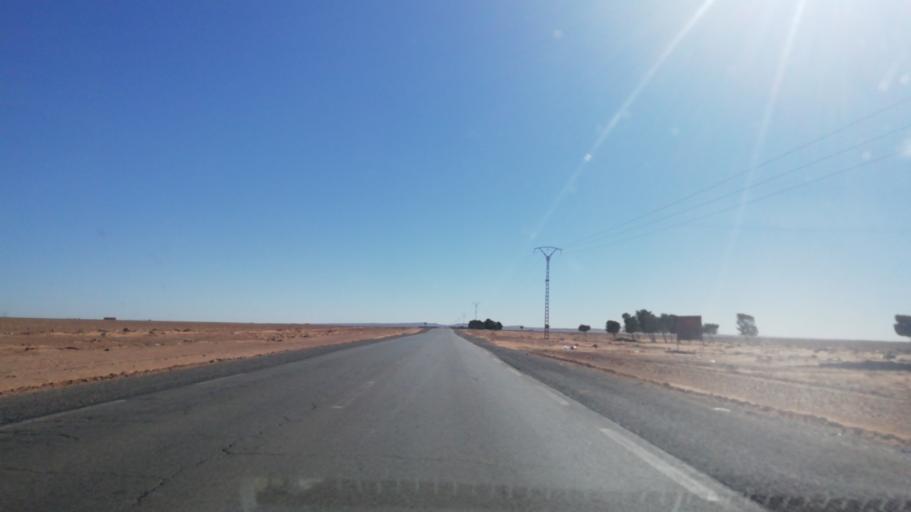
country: DZ
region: Saida
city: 'Ain el Hadjar
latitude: 34.0120
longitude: 0.1159
